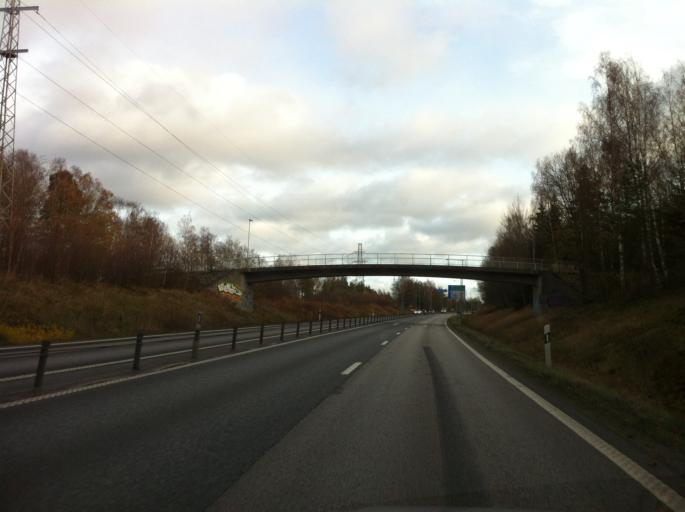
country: SE
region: Kronoberg
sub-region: Vaxjo Kommun
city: Gemla
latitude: 56.8414
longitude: 14.7103
